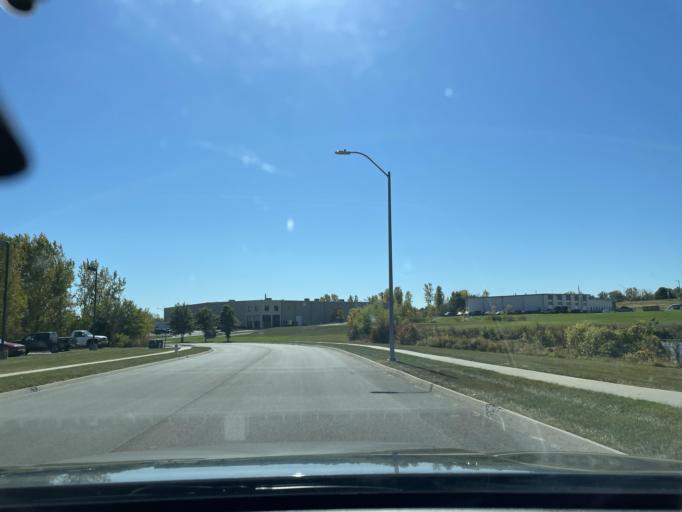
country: US
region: Missouri
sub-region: Buchanan County
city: Saint Joseph
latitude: 39.7530
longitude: -94.7648
